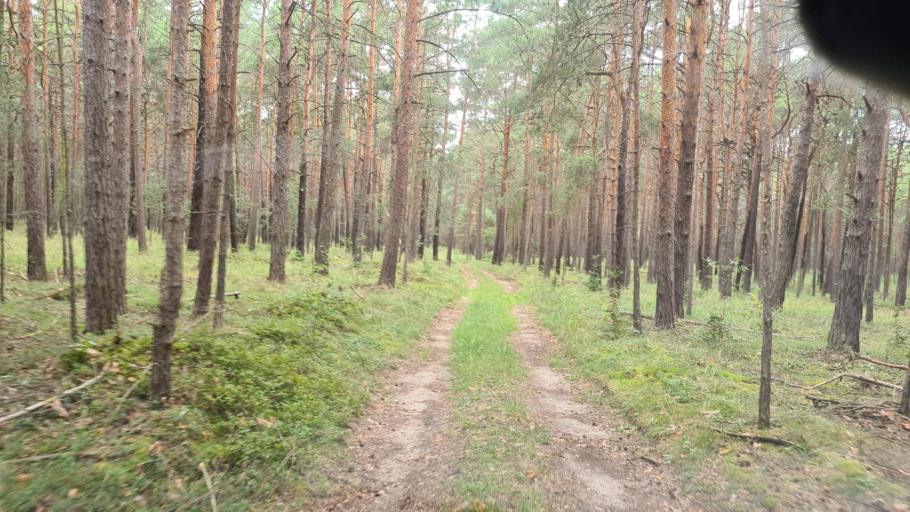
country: DE
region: Brandenburg
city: Sallgast
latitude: 51.5854
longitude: 13.8912
